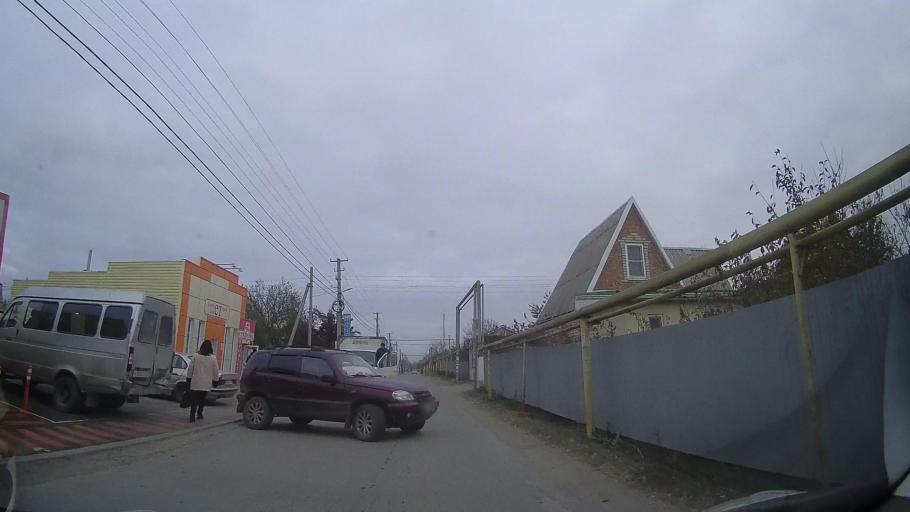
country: RU
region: Rostov
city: Bataysk
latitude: 47.0825
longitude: 39.7617
